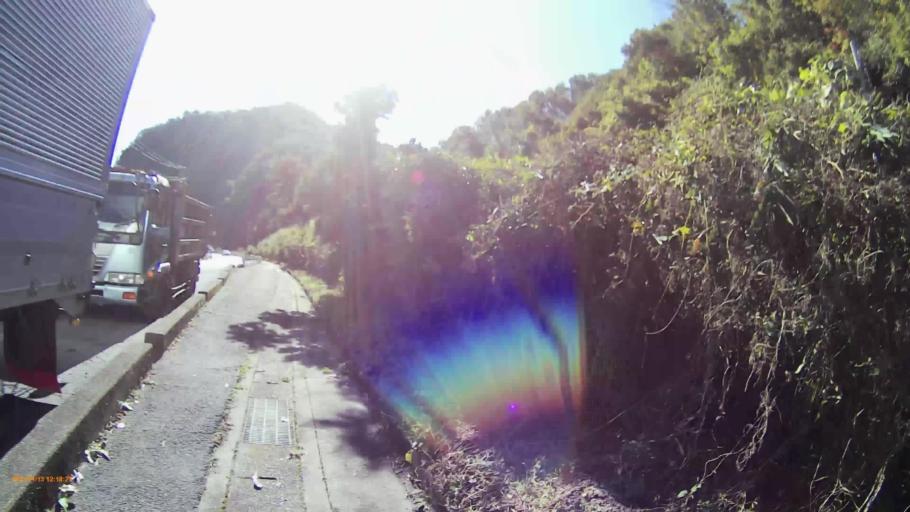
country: JP
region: Gifu
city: Inuyama
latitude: 35.4163
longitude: 136.9595
